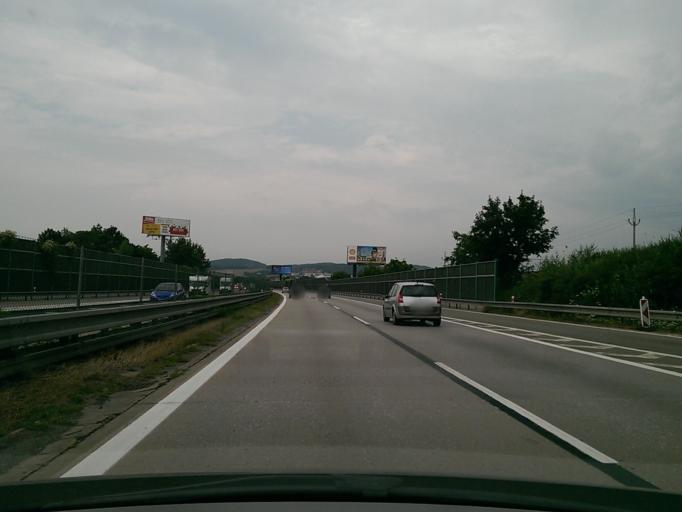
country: CZ
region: South Moravian
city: Troubsko
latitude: 49.1744
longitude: 16.5106
